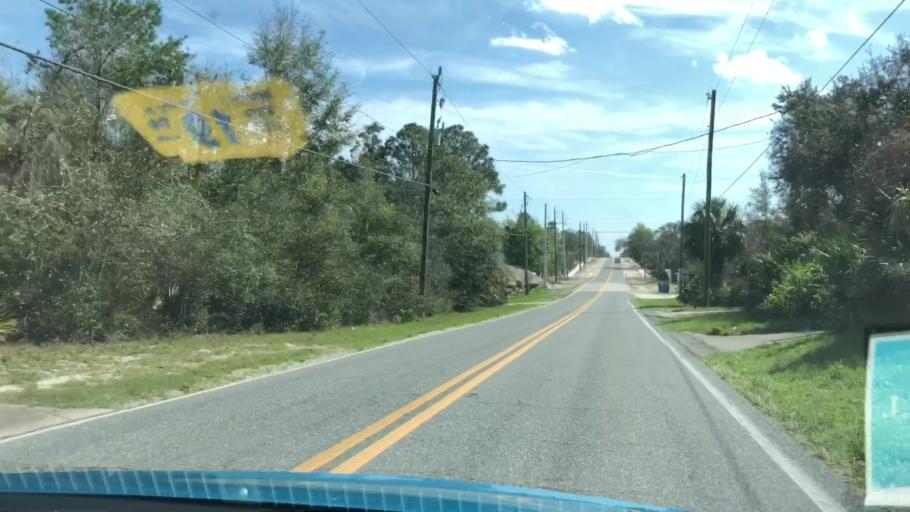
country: US
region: Florida
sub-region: Volusia County
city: Deltona
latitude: 28.8603
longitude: -81.1994
